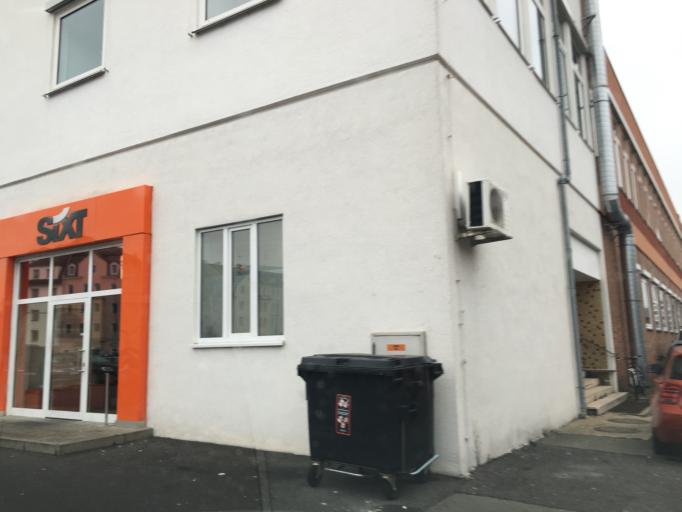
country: DE
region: Bavaria
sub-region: Regierungsbezirk Mittelfranken
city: Nuernberg
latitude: 49.4297
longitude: 11.0816
